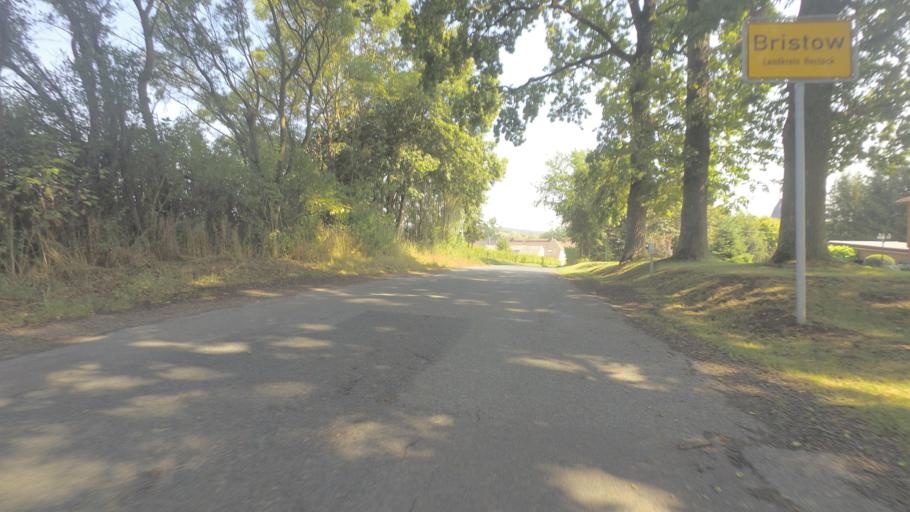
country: DE
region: Mecklenburg-Vorpommern
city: Pampow
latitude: 53.7120
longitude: 12.6212
